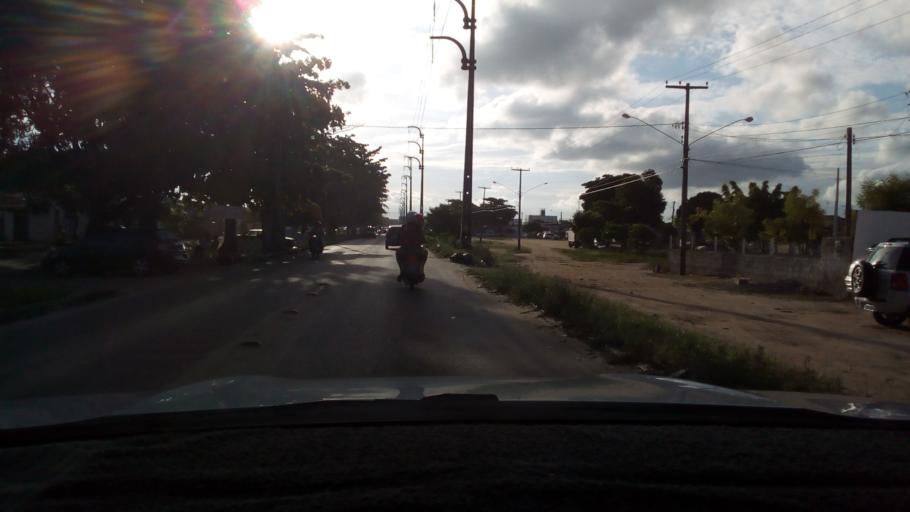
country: BR
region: Paraiba
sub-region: Joao Pessoa
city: Joao Pessoa
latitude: -7.1802
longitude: -34.8672
